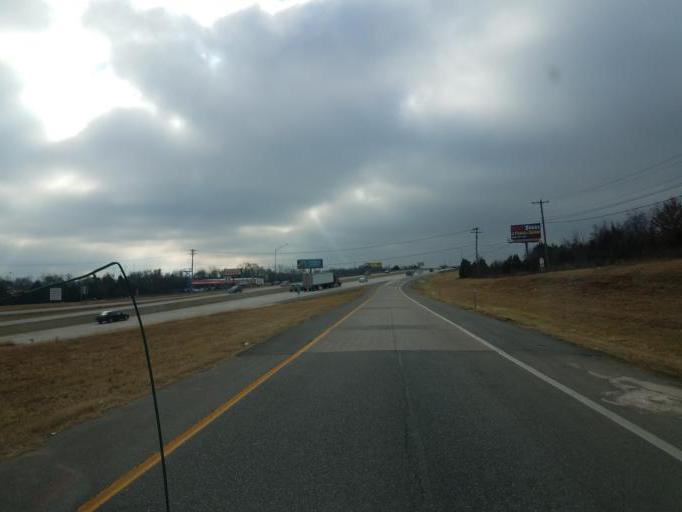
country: US
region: Missouri
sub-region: Greene County
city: Springfield
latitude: 37.2383
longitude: -93.2253
